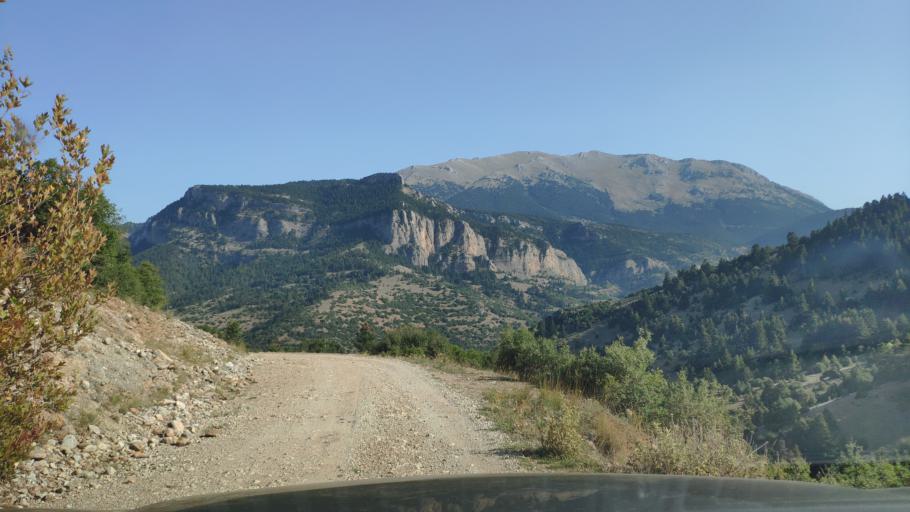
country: GR
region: West Greece
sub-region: Nomos Achaias
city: Aiyira
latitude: 37.9856
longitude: 22.3453
